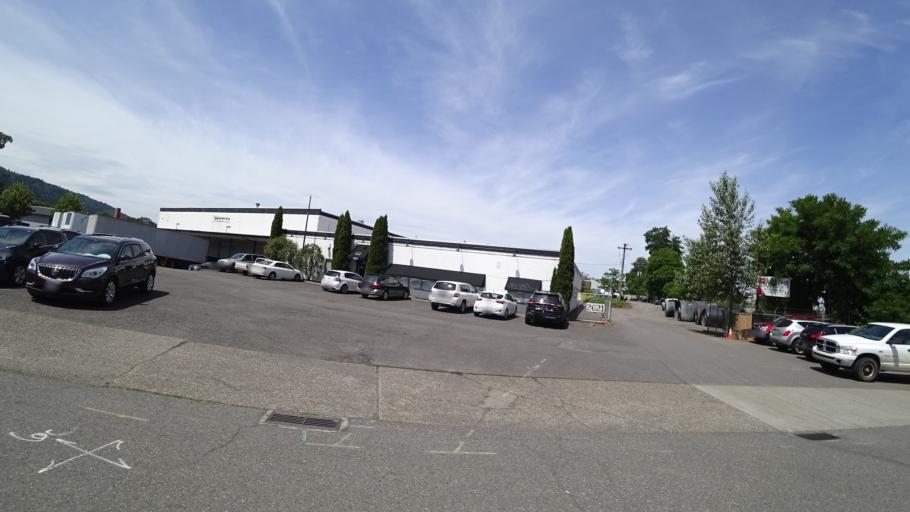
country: US
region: Oregon
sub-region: Multnomah County
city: Portland
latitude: 45.5412
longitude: -122.7068
